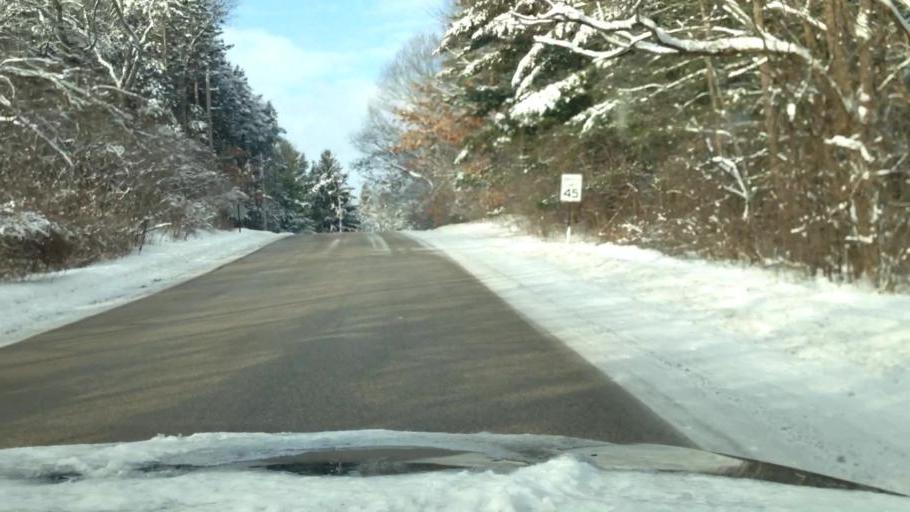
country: US
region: Wisconsin
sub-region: Walworth County
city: East Troy
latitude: 42.8111
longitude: -88.4266
